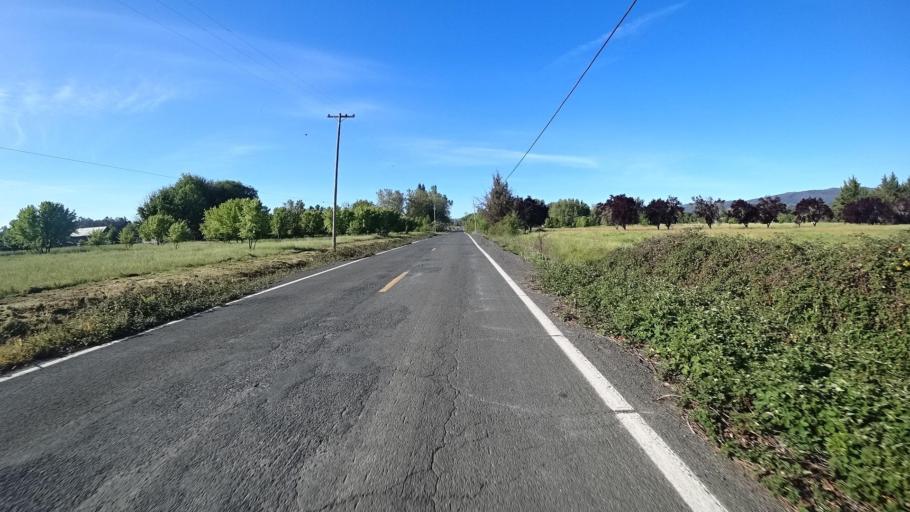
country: US
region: California
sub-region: Lake County
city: North Lakeport
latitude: 39.0853
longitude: -122.9498
